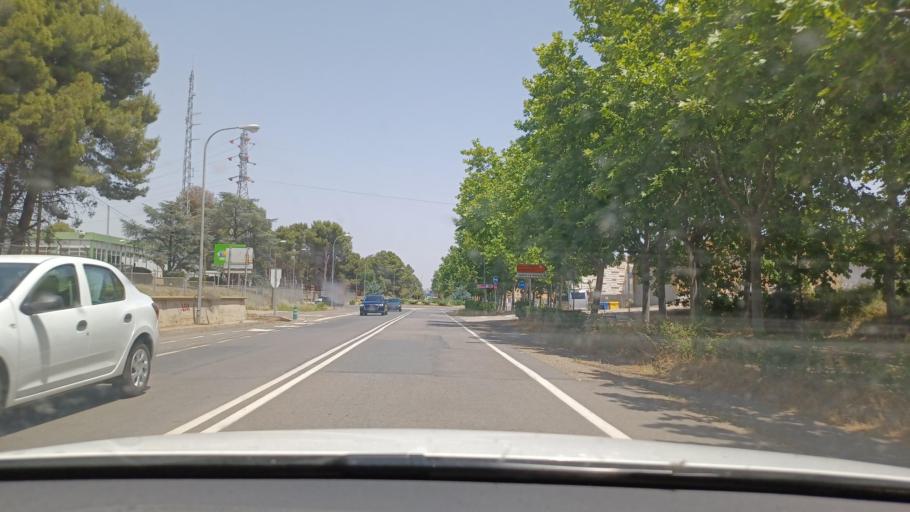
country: ES
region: Navarre
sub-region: Provincia de Navarra
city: Tudela
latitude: 42.0499
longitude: -1.6146
